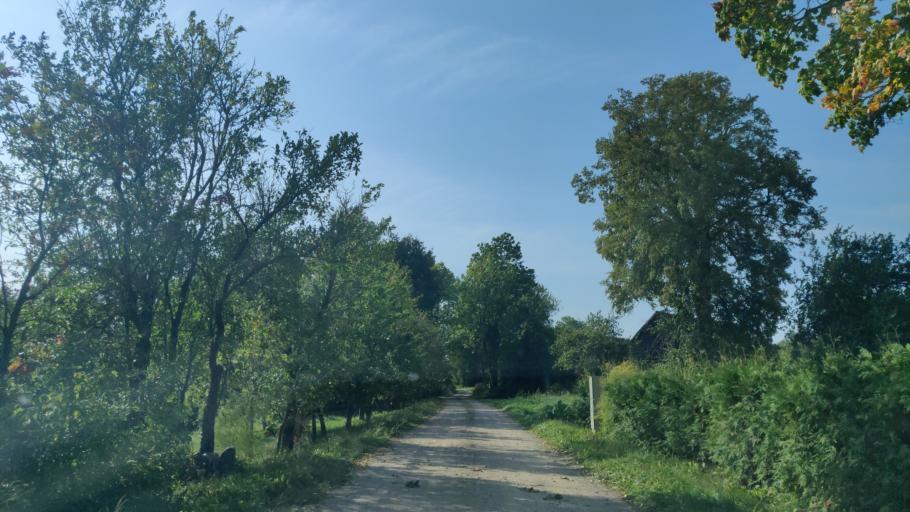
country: LT
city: Sirvintos
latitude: 54.9625
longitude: 24.7850
